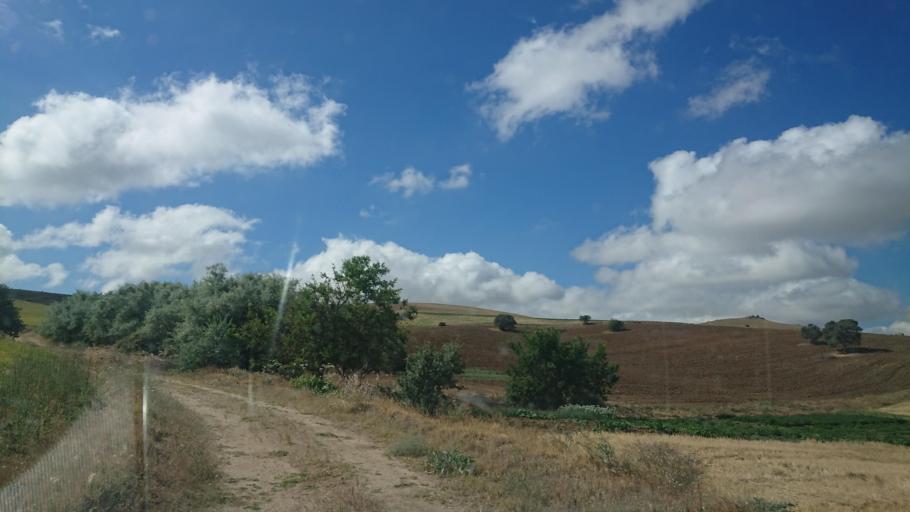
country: TR
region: Aksaray
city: Agacoren
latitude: 38.8433
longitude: 33.9367
